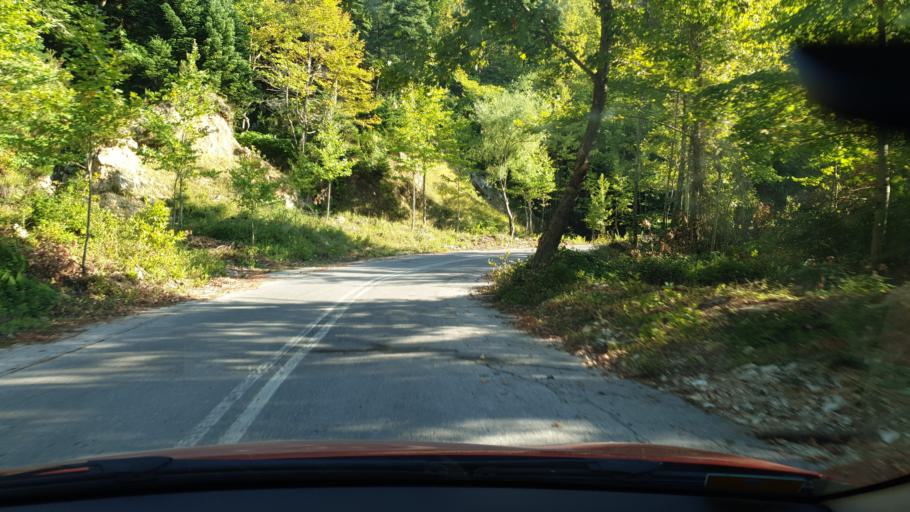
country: GR
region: Central Greece
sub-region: Nomos Evvoias
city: Yimnon
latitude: 38.6012
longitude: 23.9132
